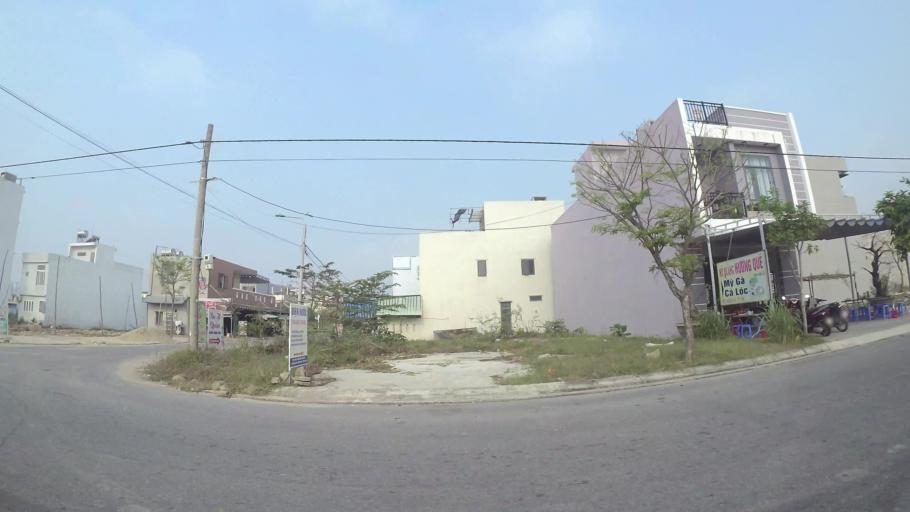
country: VN
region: Da Nang
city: Ngu Hanh Son
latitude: 16.0093
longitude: 108.2291
